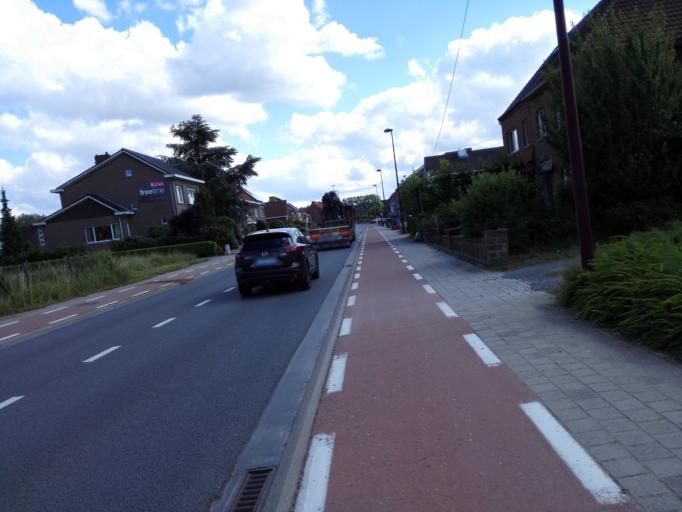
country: BE
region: Flanders
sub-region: Provincie Vlaams-Brabant
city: Aarschot
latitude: 50.9948
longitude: 4.8427
